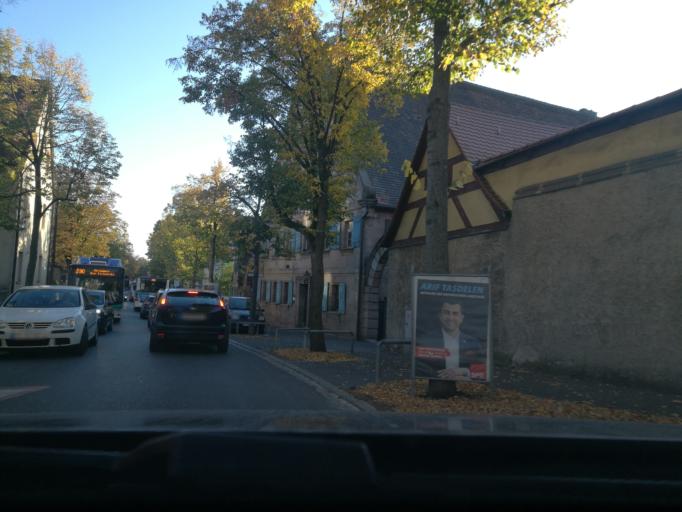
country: DE
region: Bavaria
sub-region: Regierungsbezirk Mittelfranken
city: Furth
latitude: 49.5297
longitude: 11.0112
